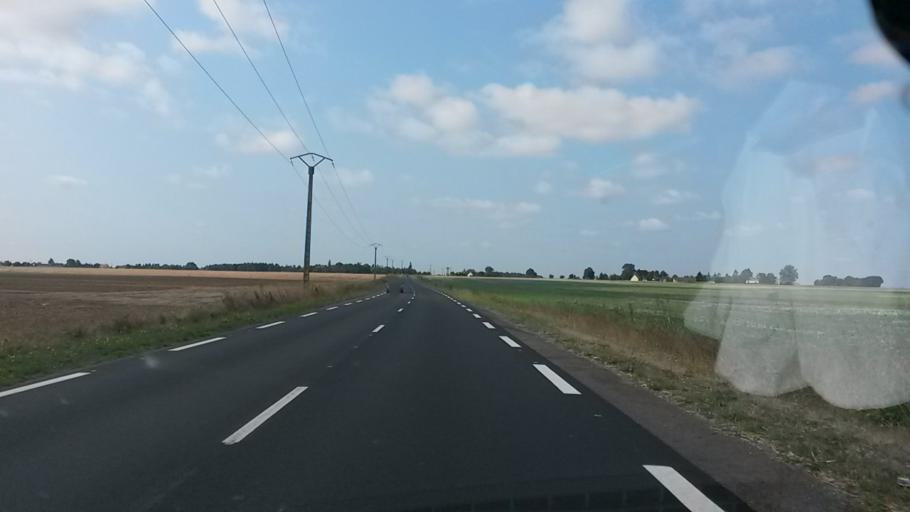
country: FR
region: Haute-Normandie
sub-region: Departement de l'Eure
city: Verneuil-sur-Avre
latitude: 48.7849
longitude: 0.9811
